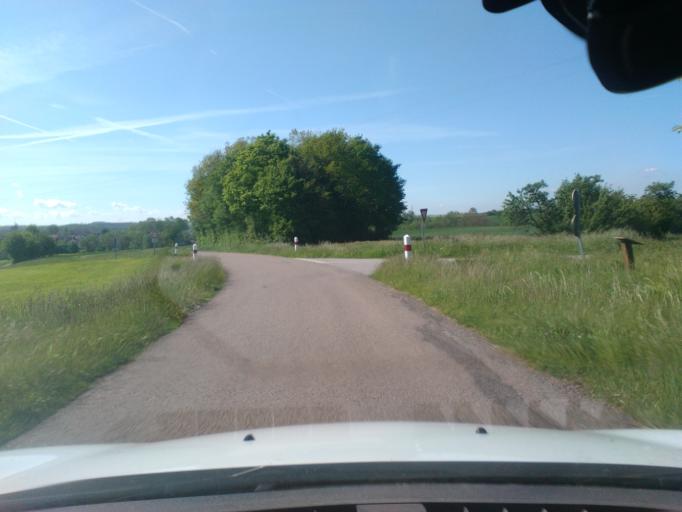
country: FR
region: Lorraine
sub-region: Departement des Vosges
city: Mirecourt
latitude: 48.3080
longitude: 6.1671
